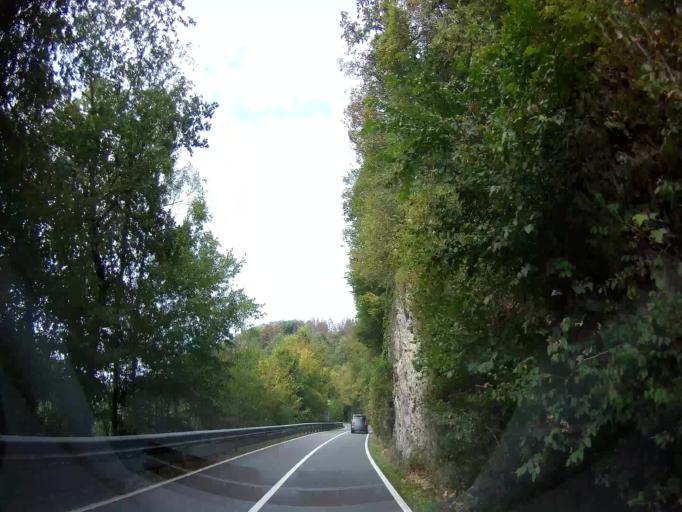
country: BE
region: Wallonia
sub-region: Province de Liege
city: Hamoir
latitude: 50.3881
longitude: 5.5405
